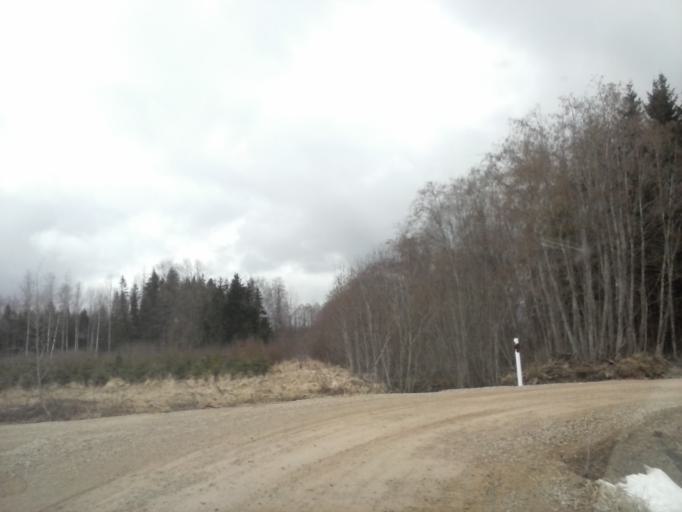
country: EE
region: Jogevamaa
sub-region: Mustvee linn
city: Mustvee
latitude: 59.0953
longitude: 26.8202
